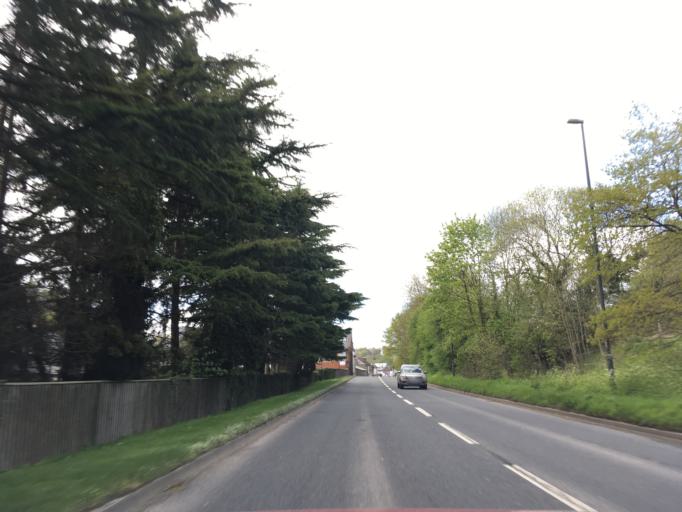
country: GB
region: England
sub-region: Gloucestershire
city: Brimscombe
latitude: 51.7289
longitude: -2.2034
